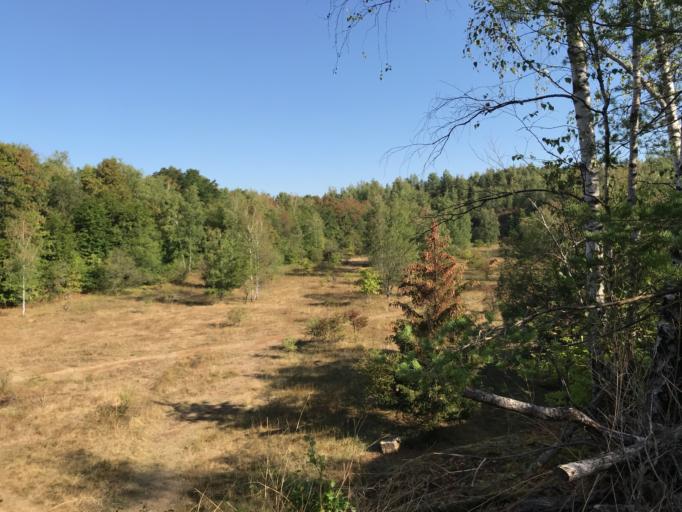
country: LU
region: Luxembourg
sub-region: Canton d'Esch-sur-Alzette
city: Niedercorn
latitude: 49.5412
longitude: 5.8771
